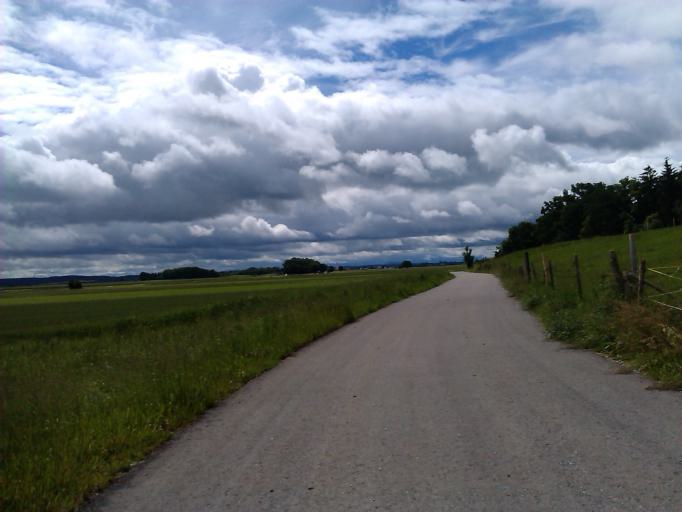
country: DE
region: Bavaria
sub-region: Swabia
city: Bad Worishofen
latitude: 47.9980
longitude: 10.6035
